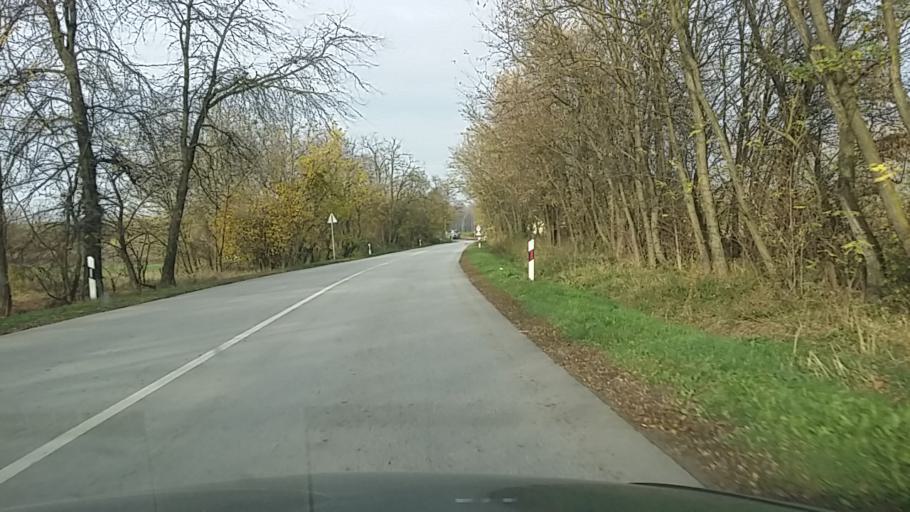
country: HU
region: Szabolcs-Szatmar-Bereg
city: Nyirbogdany
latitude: 48.0624
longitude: 21.8595
